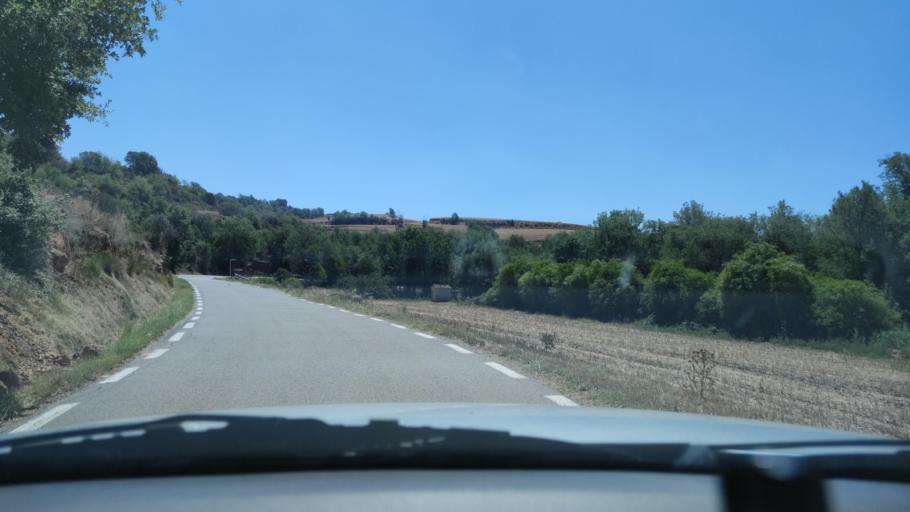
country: ES
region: Catalonia
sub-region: Provincia de Lleida
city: Tora de Riubregos
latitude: 41.8376
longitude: 1.4222
